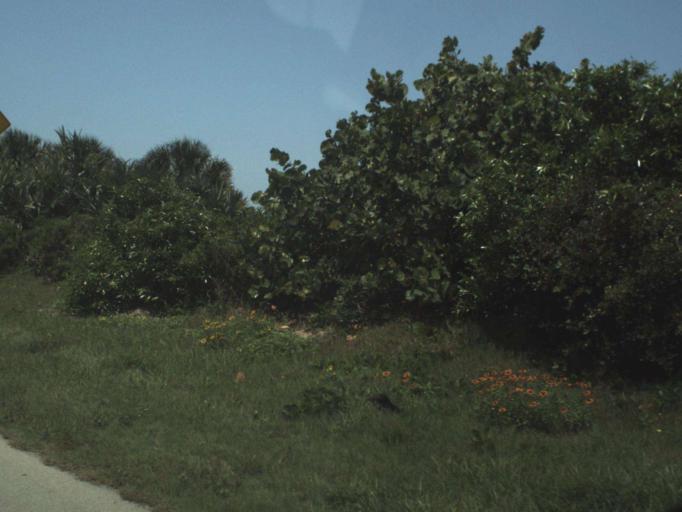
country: US
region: Florida
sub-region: Brevard County
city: Melbourne Beach
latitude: 28.0376
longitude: -80.5434
